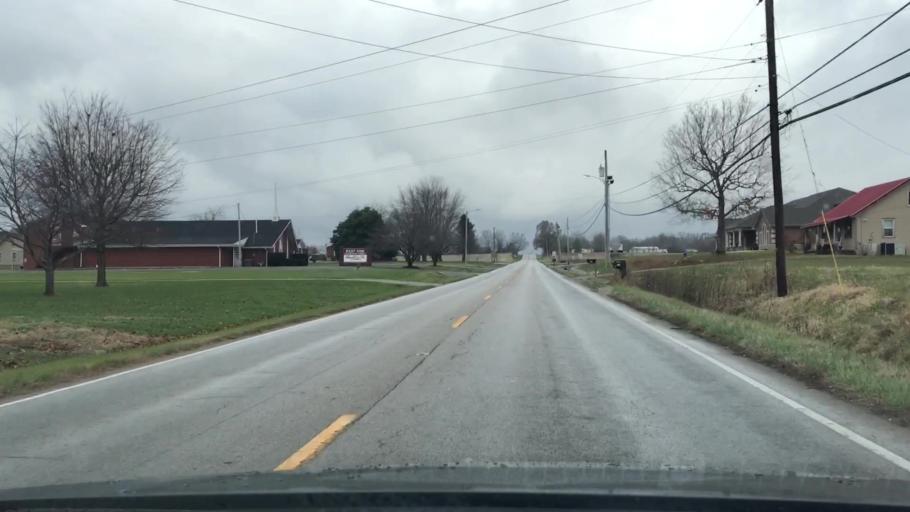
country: US
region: Kentucky
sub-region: Todd County
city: Elkton
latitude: 36.8143
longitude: -87.1747
